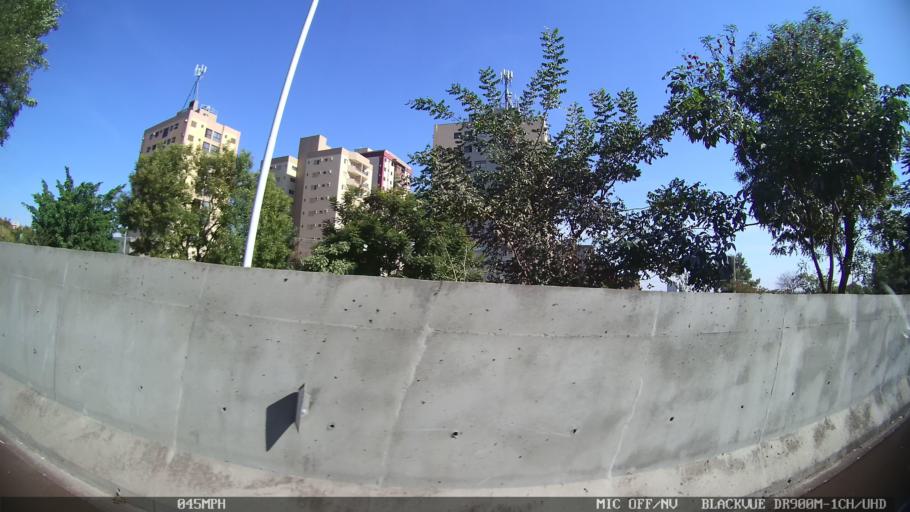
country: BR
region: Sao Paulo
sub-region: Ribeirao Preto
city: Ribeirao Preto
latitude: -21.1896
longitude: -47.7816
